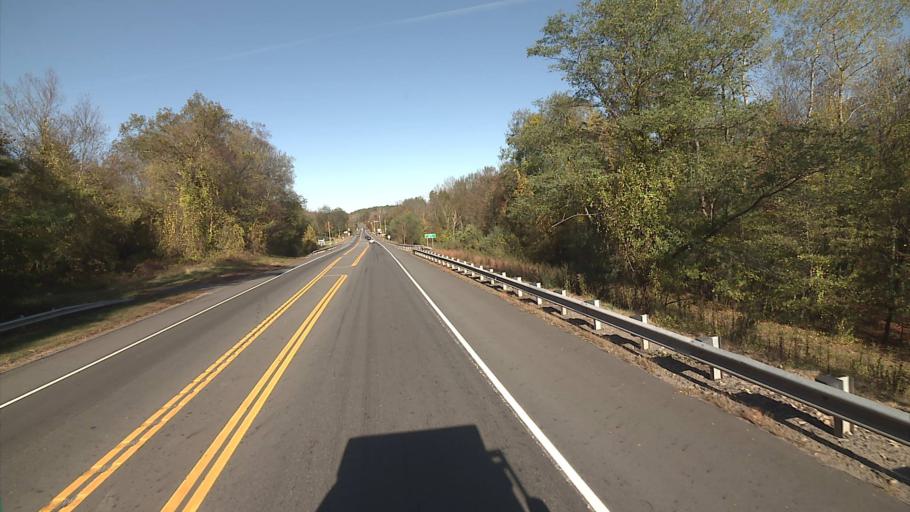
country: US
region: Connecticut
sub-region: Tolland County
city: Coventry Lake
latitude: 41.7304
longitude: -72.3541
